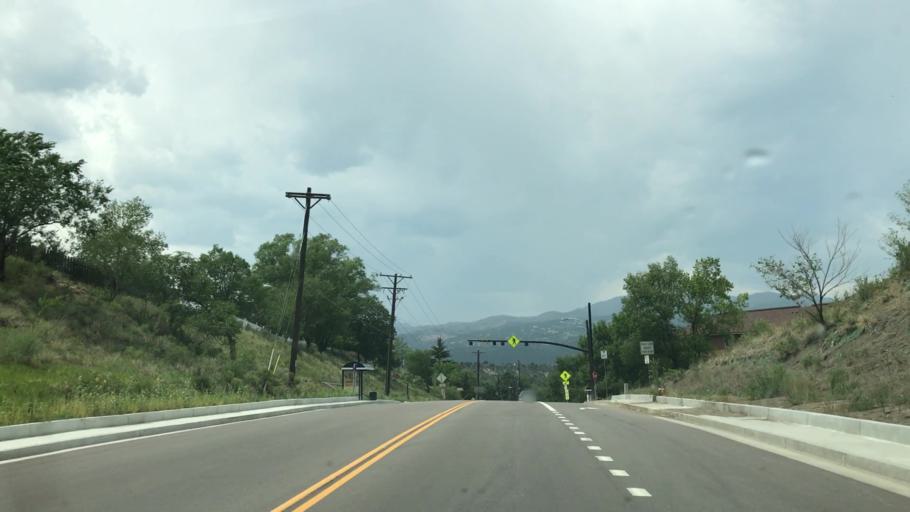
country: US
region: Colorado
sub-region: El Paso County
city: Colorado Springs
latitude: 38.8518
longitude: -104.8612
